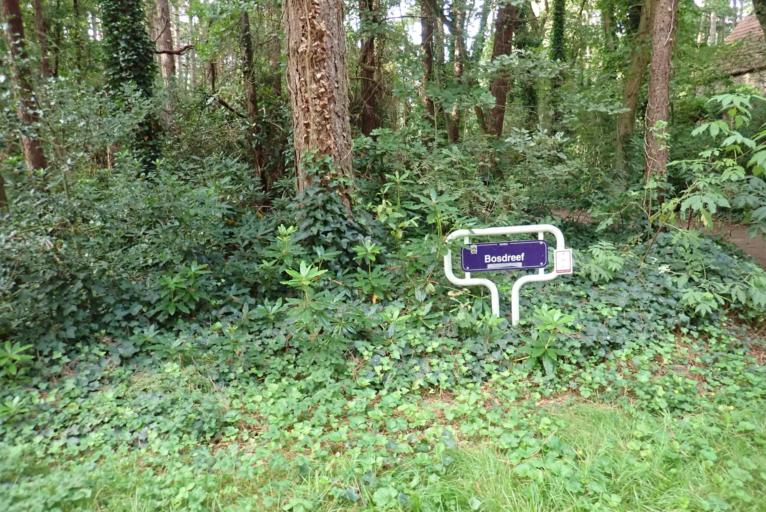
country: BE
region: Flanders
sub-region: Provincie Antwerpen
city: Essen
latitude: 51.4633
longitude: 4.5267
